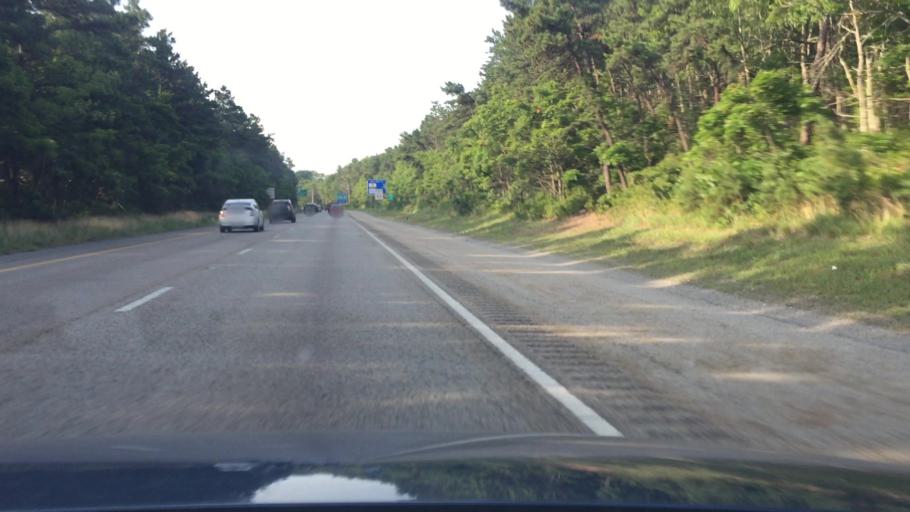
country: US
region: Massachusetts
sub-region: Barnstable County
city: Sagamore
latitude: 41.7917
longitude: -70.5458
